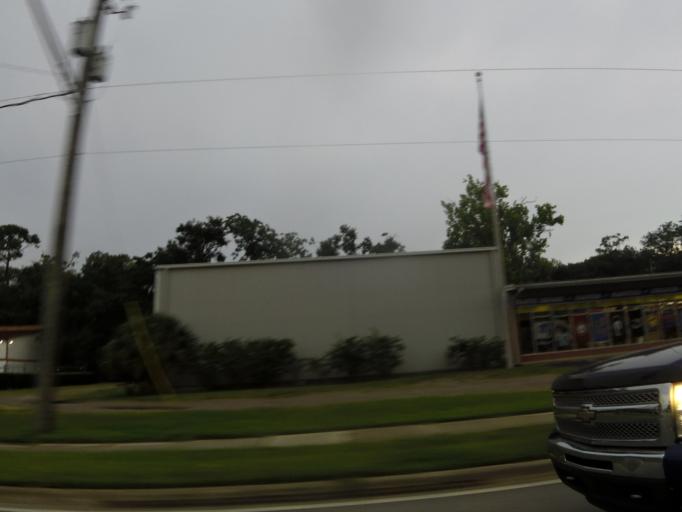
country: US
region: Florida
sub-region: Duval County
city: Jacksonville
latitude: 30.2849
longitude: -81.5869
